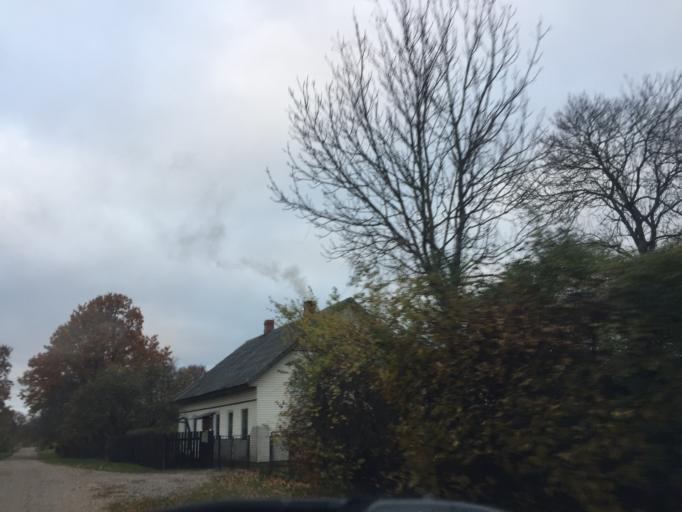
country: LV
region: Skrunda
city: Skrunda
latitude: 56.6770
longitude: 22.0250
